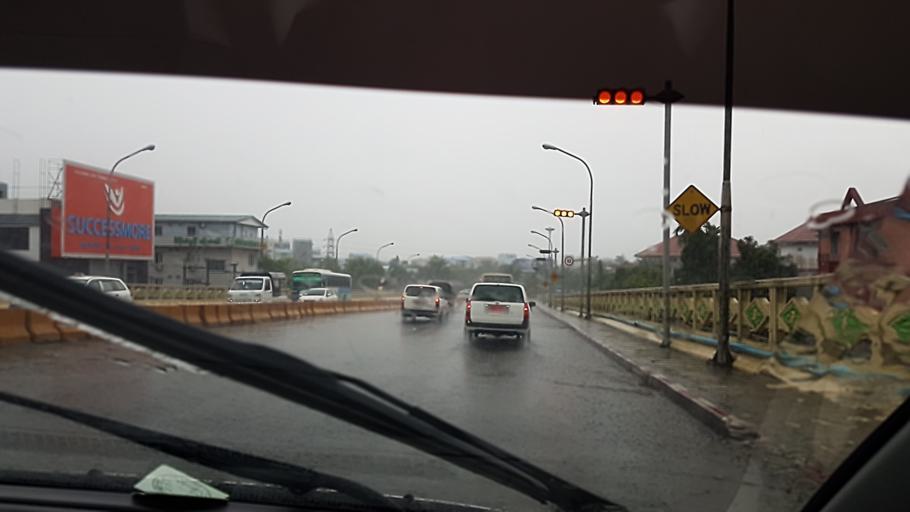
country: MM
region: Yangon
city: Yangon
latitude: 16.7806
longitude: 96.1851
